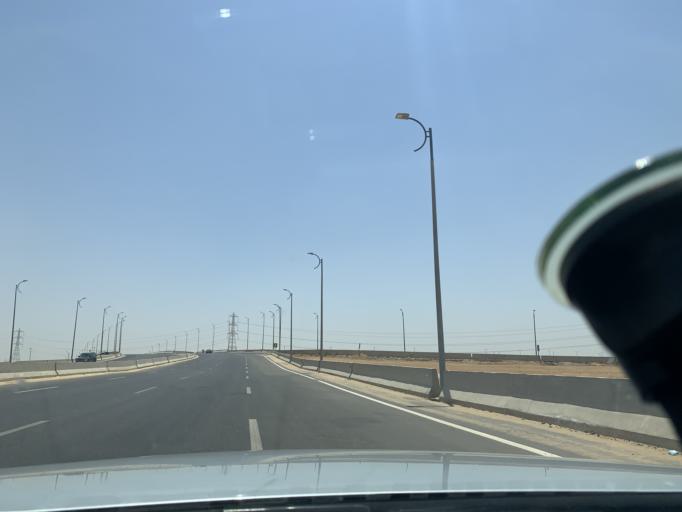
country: EG
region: Muhafazat al Qahirah
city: Halwan
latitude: 29.9695
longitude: 31.4693
